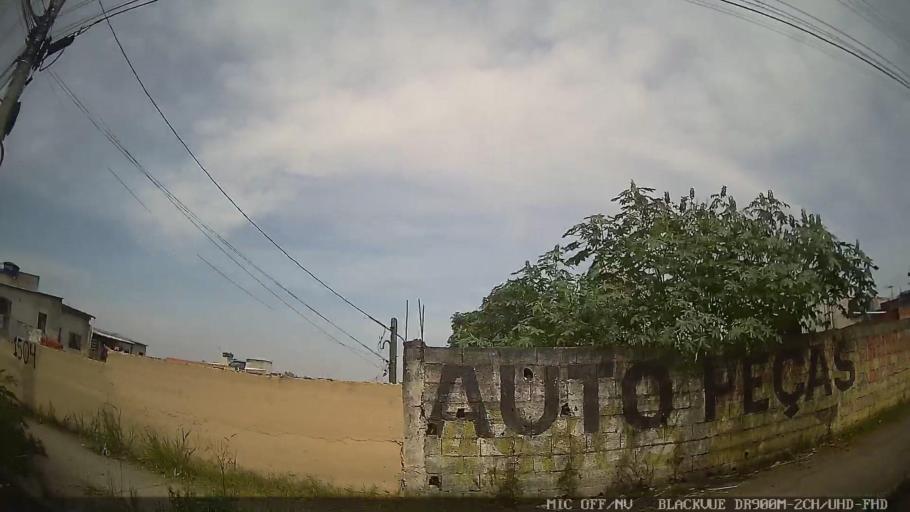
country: BR
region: Sao Paulo
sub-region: Ferraz De Vasconcelos
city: Ferraz de Vasconcelos
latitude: -23.5274
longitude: -46.3628
